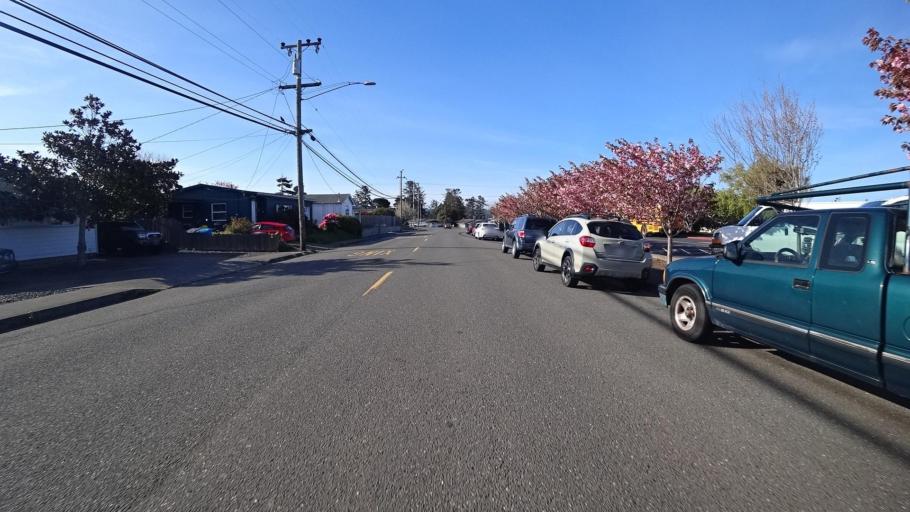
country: US
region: California
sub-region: Humboldt County
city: Bayview
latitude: 40.7586
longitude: -124.1811
